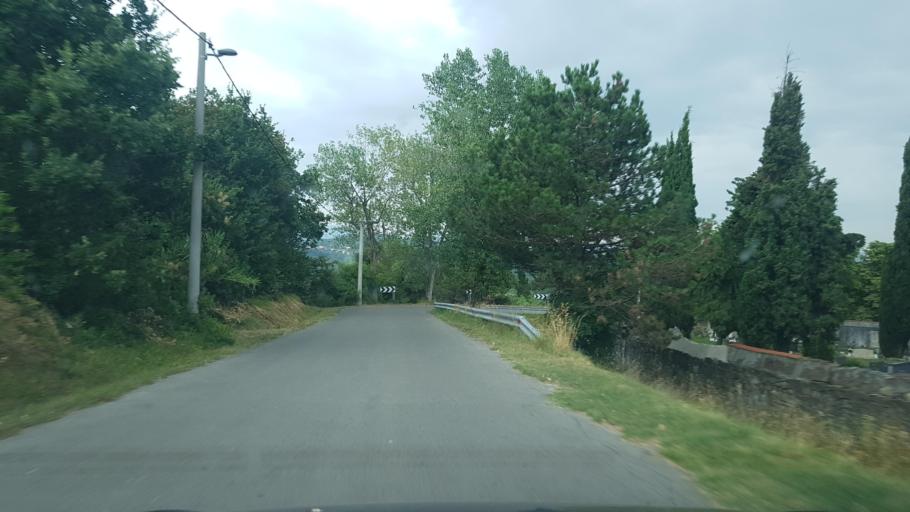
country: SI
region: Koper-Capodistria
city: Hrvatini
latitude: 45.5963
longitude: 13.7469
